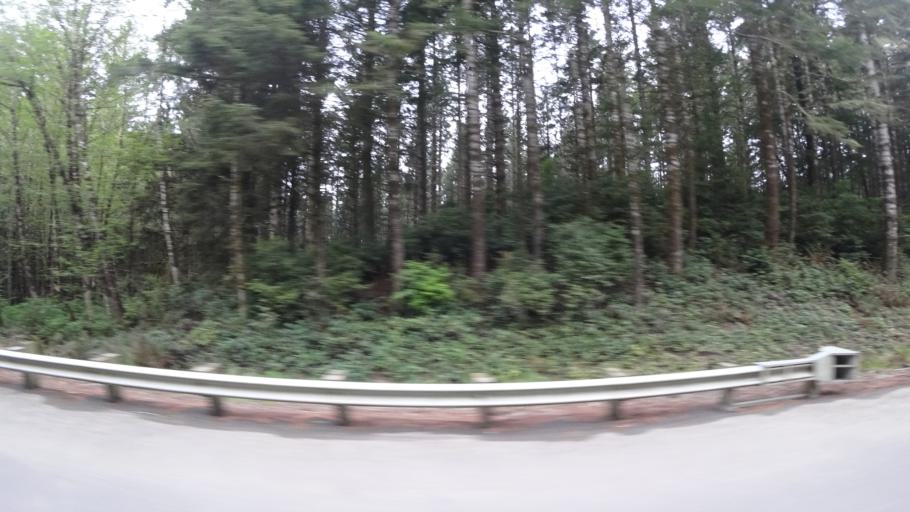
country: US
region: Oregon
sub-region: Coos County
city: Coquille
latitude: 43.2077
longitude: -124.3065
